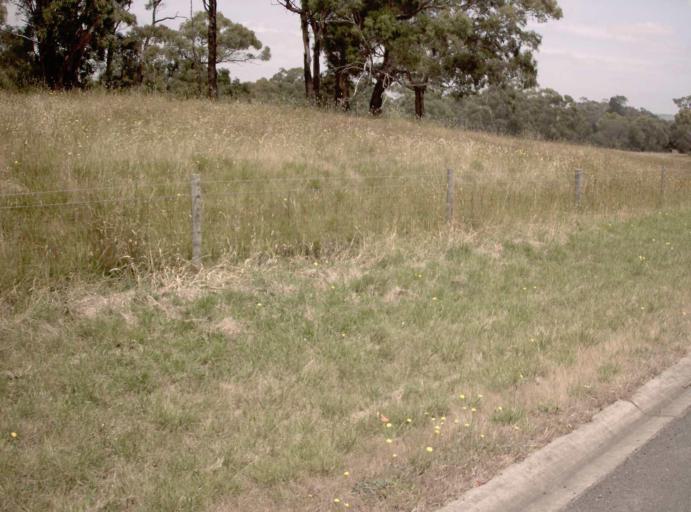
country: AU
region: Victoria
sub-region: Latrobe
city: Traralgon
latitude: -38.2508
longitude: 146.5635
